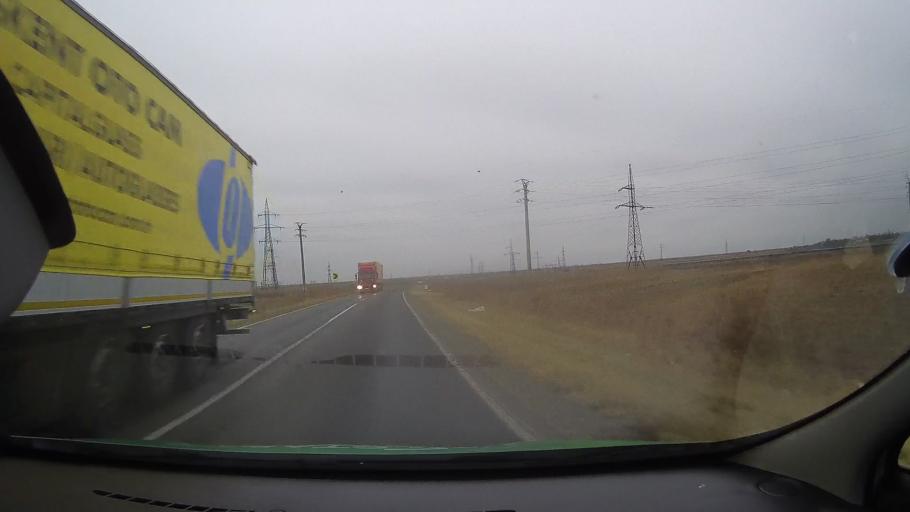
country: RO
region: Braila
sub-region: Comuna Baraganul
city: Baraganul
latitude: 44.7949
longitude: 27.5113
